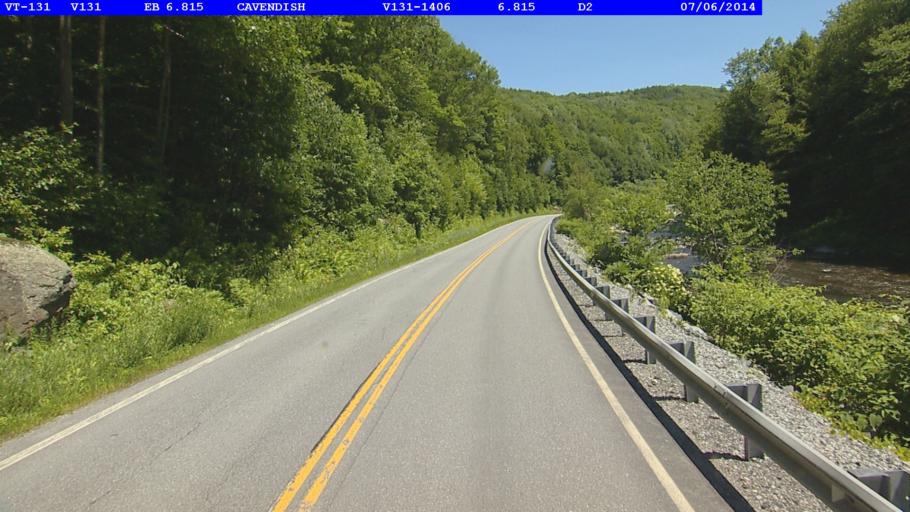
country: US
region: Vermont
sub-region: Windsor County
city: Springfield
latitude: 43.3919
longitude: -72.5533
